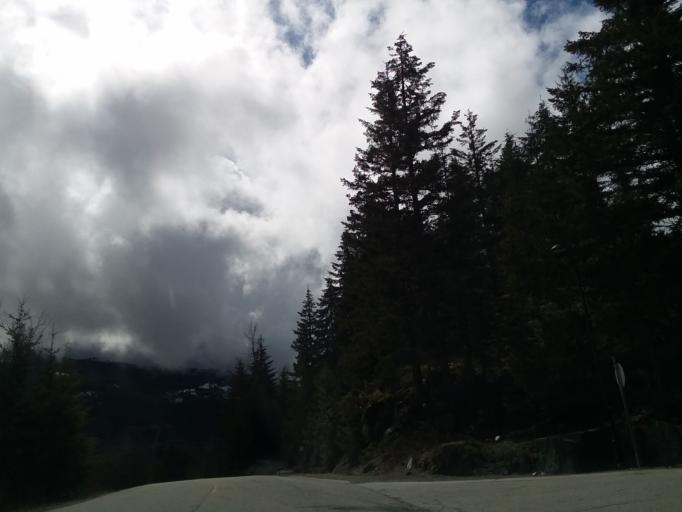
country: CA
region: British Columbia
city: Whistler
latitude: 50.1013
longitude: -123.0006
